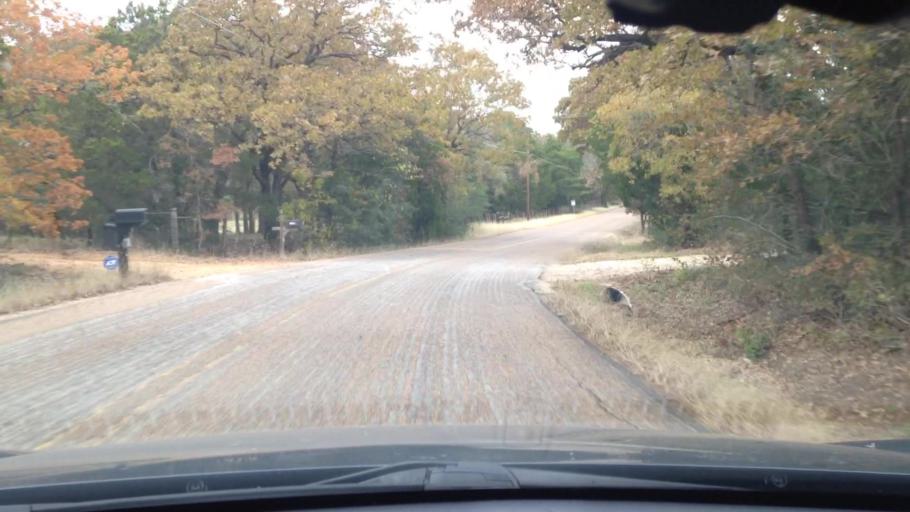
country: US
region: Texas
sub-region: Bastrop County
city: Bastrop
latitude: 30.1342
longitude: -97.2857
